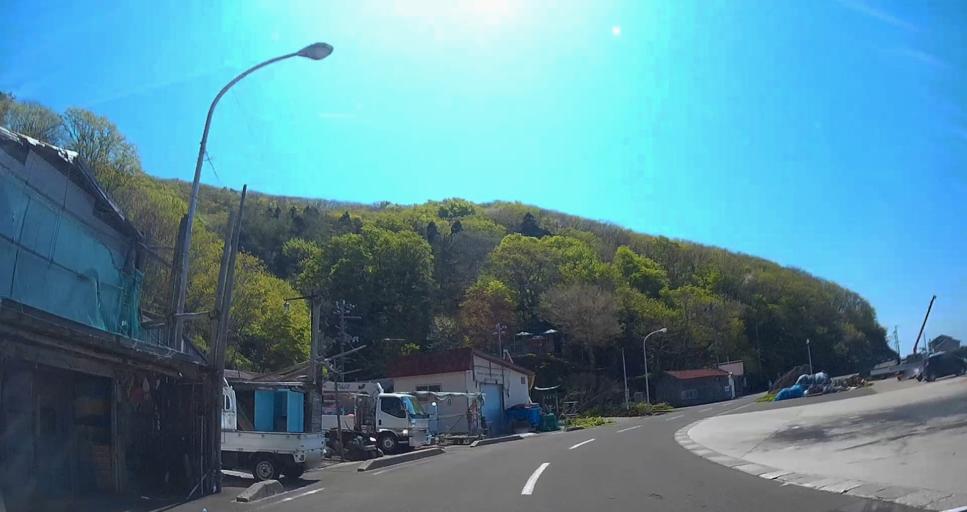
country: JP
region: Aomori
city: Aomori Shi
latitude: 41.1421
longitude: 140.7740
